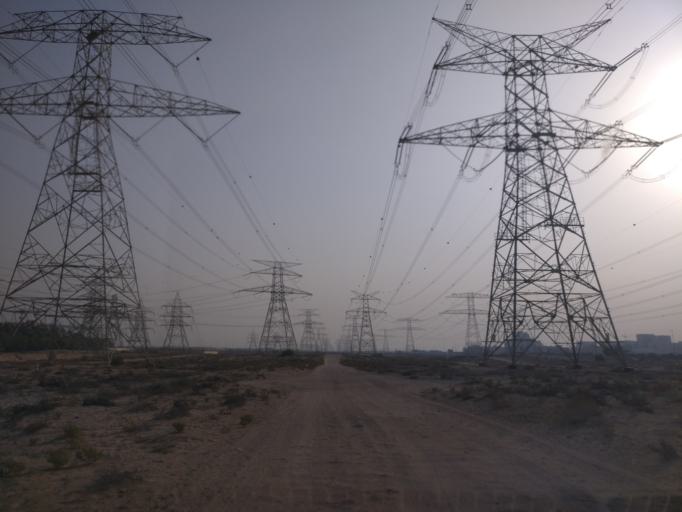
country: AE
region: Dubai
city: Dubai
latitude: 25.0605
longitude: 55.1929
